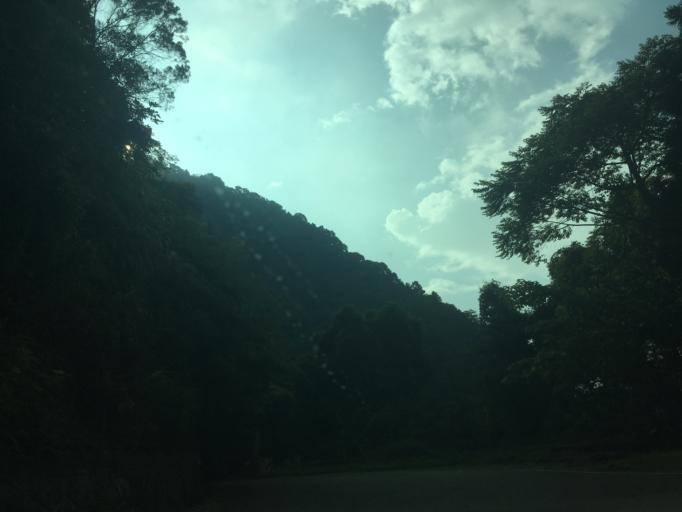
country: TW
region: Taiwan
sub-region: Miaoli
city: Miaoli
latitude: 24.4053
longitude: 120.9760
